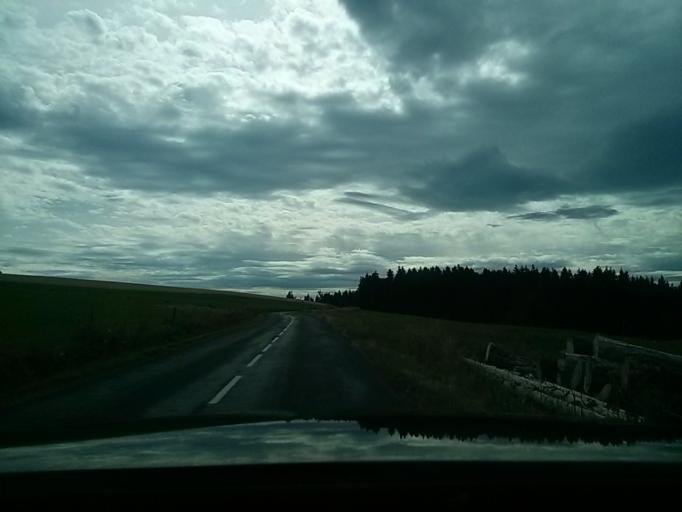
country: FR
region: Rhone-Alpes
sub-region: Departement de la Loire
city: Saint-Genest-Malifaux
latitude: 45.3590
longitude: 4.4746
